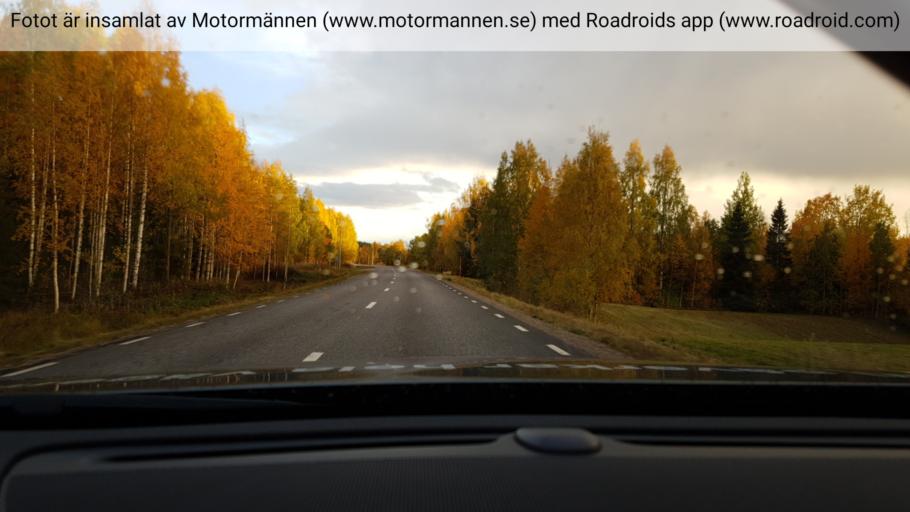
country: SE
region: Norrbotten
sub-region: Overkalix Kommun
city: OEverkalix
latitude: 66.5422
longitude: 22.7538
